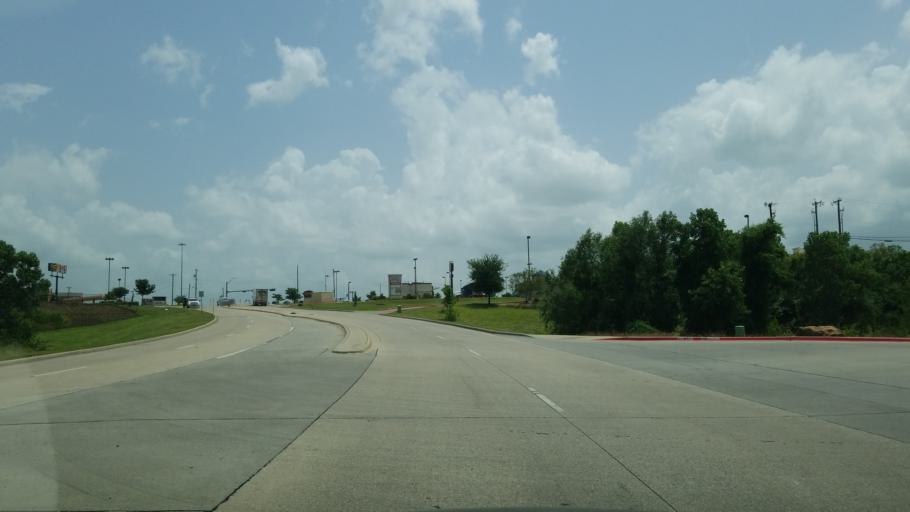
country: US
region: Texas
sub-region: Dallas County
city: Cockrell Hill
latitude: 32.7700
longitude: -96.8968
